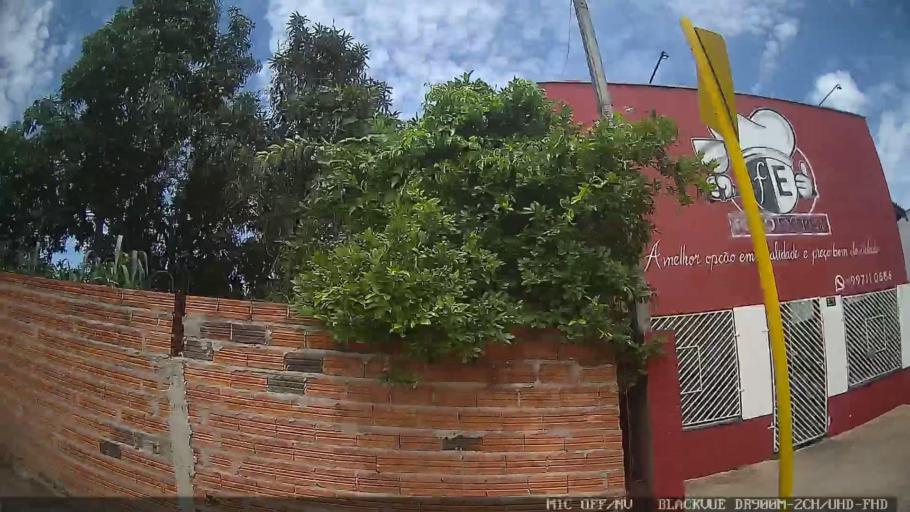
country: BR
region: Sao Paulo
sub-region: Laranjal Paulista
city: Laranjal Paulista
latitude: -23.0404
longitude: -47.8232
